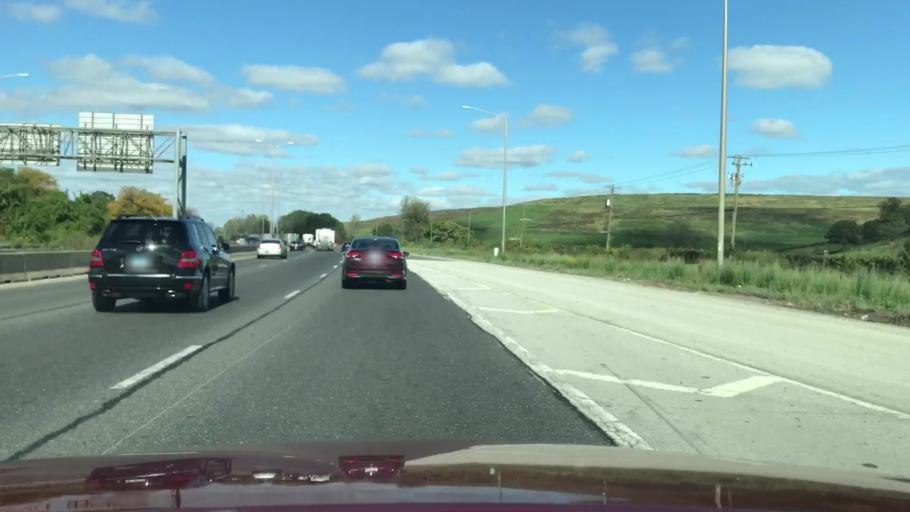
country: US
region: Illinois
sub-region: Cook County
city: Burnham
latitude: 41.6482
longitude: -87.5789
